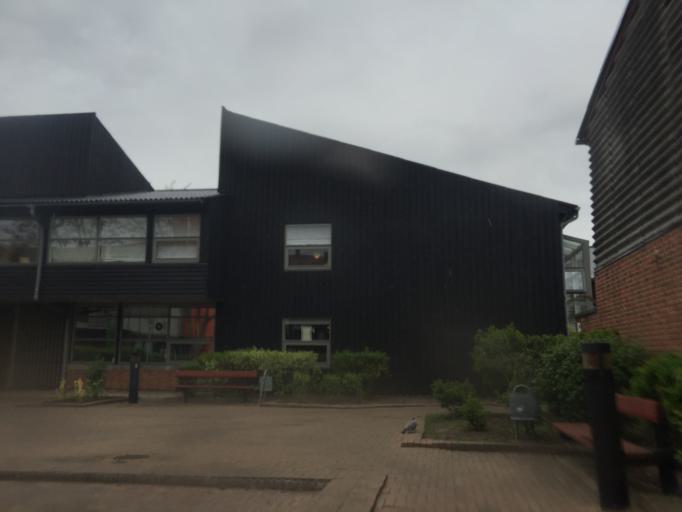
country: DK
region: Capital Region
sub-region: Kobenhavn
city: Vanlose
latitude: 55.6833
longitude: 12.5087
